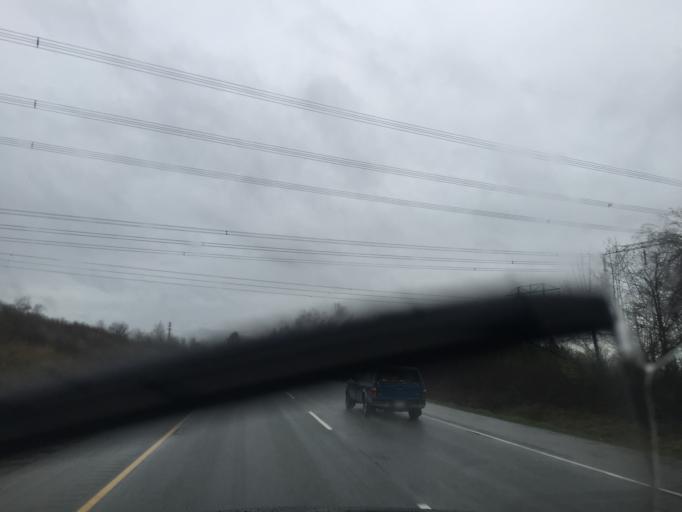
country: CA
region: British Columbia
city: Aldergrove
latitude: 49.0705
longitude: -122.4143
